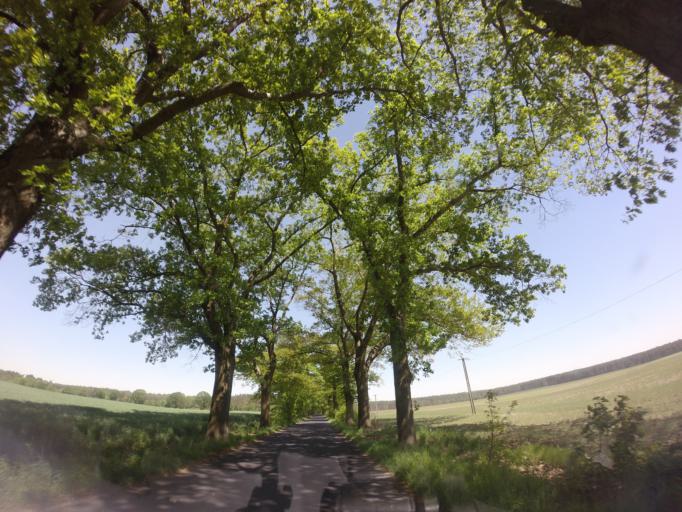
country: PL
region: West Pomeranian Voivodeship
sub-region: Powiat mysliborski
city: Nowogrodek Pomorski
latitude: 52.9176
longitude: 15.1323
